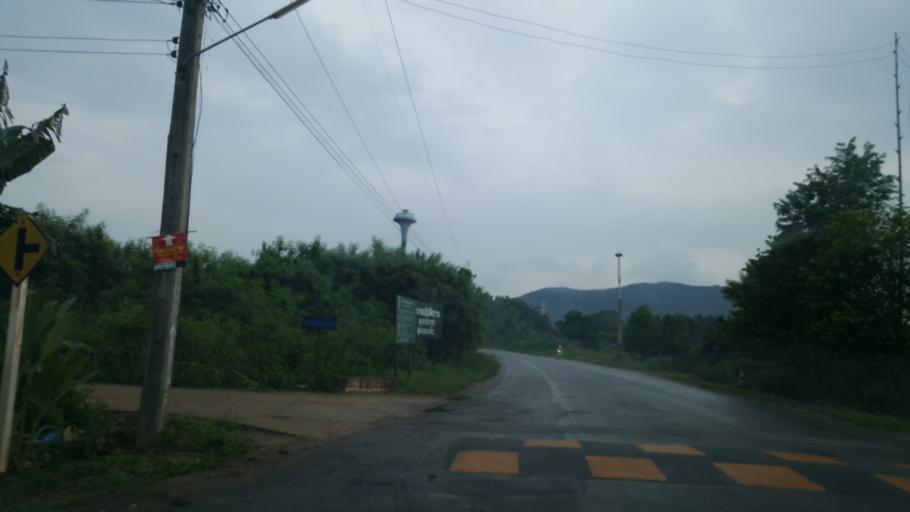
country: TH
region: Chon Buri
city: Sattahip
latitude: 12.7198
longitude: 100.9177
